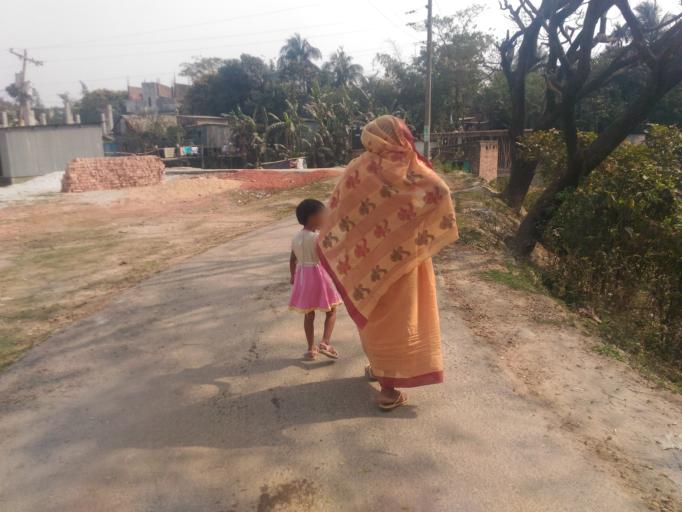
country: BD
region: Dhaka
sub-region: Dhaka
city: Dhaka
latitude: 23.6703
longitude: 90.4210
